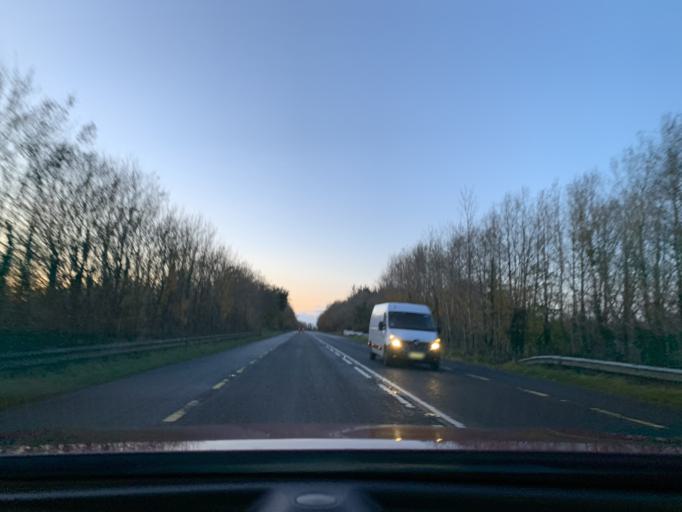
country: IE
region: Connaught
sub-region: County Leitrim
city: Carrick-on-Shannon
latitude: 53.9348
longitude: -8.0489
